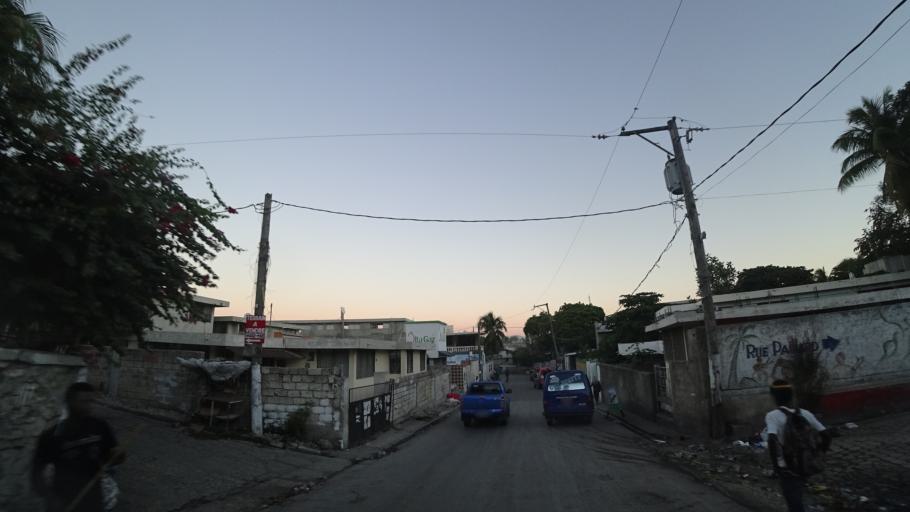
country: HT
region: Ouest
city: Delmas 73
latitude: 18.5445
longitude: -72.3163
